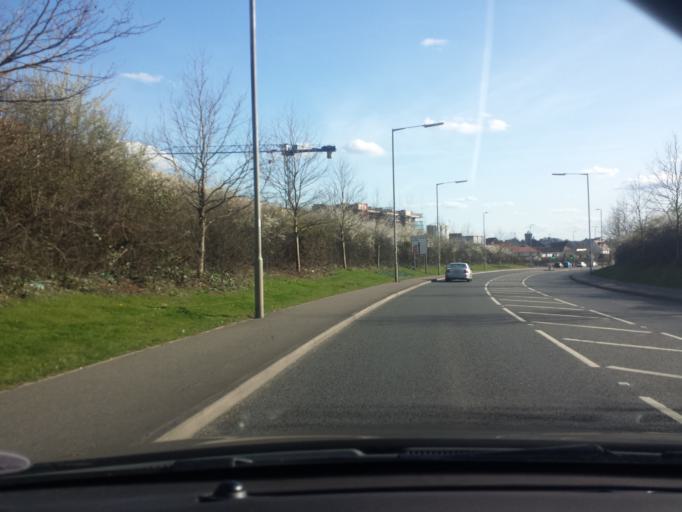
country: GB
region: England
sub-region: Essex
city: Colchester
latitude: 51.9048
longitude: 0.8985
